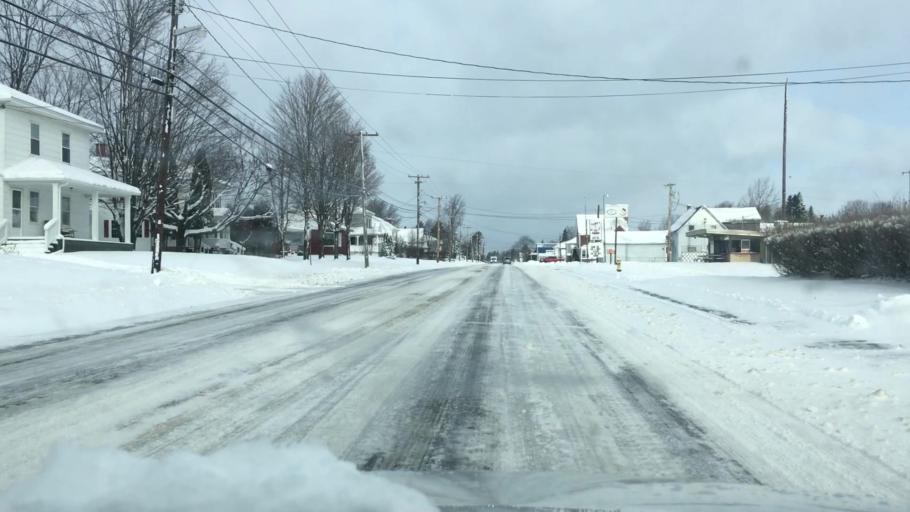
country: US
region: Maine
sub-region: Aroostook County
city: Van Buren
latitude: 47.1651
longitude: -67.9422
